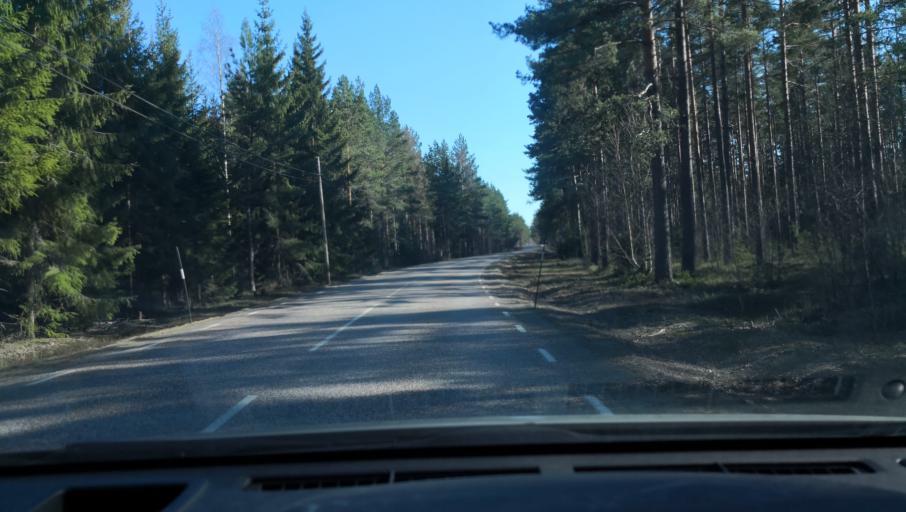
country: SE
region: Dalarna
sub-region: Avesta Kommun
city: Avesta
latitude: 60.0076
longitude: 16.3450
